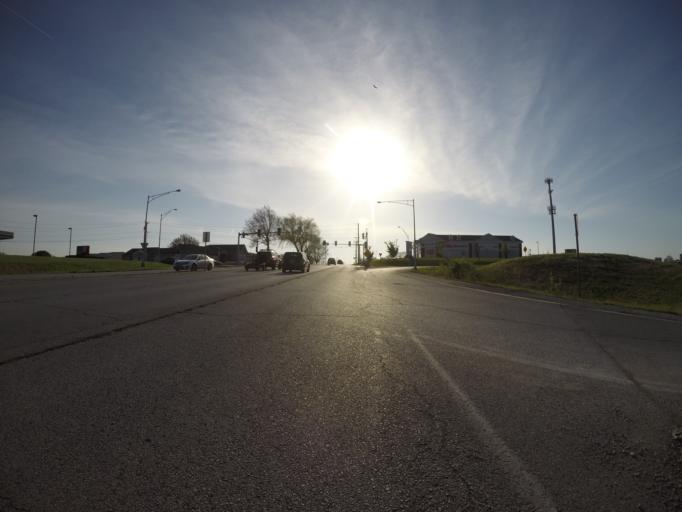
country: US
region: Missouri
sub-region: Jackson County
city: Lees Summit
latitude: 38.9111
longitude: -94.3928
